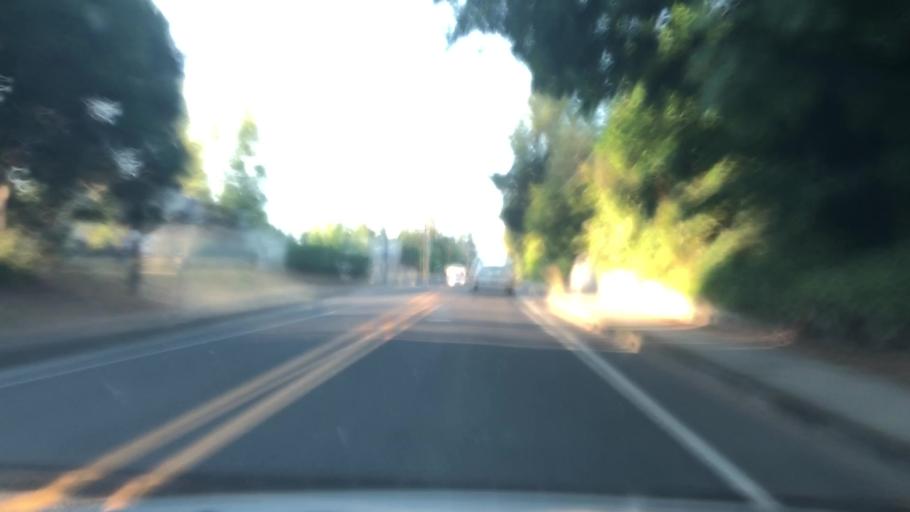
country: US
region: Oregon
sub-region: Clackamas County
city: Oak Grove
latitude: 45.4142
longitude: -122.6455
